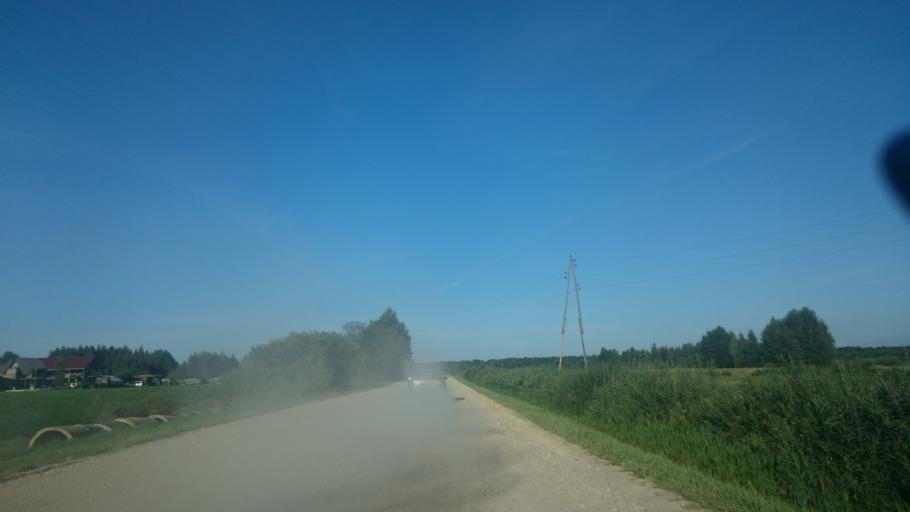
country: LV
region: Riga
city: Jaunciems
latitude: 57.0943
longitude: 24.1884
